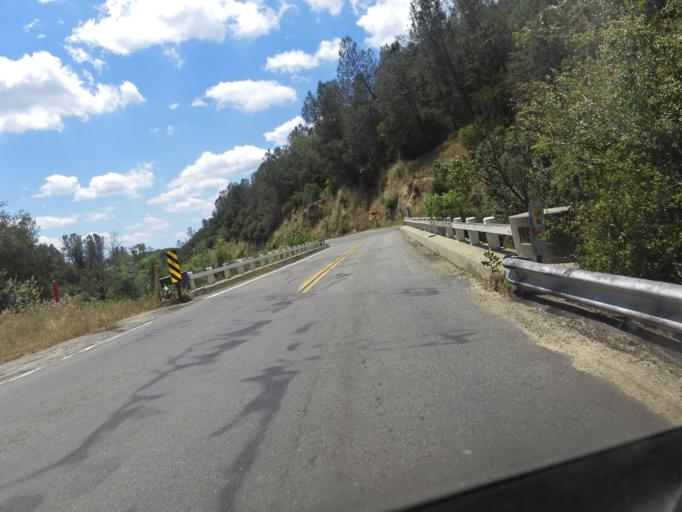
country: US
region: California
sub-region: Madera County
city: Coarsegold
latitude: 37.1790
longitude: -119.6292
